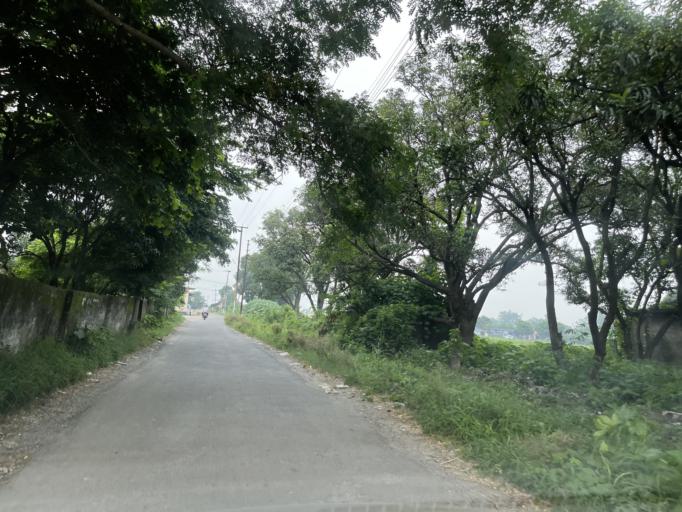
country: IN
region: Uttarakhand
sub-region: Naini Tal
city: Haldwani
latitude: 29.1719
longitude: 79.4852
